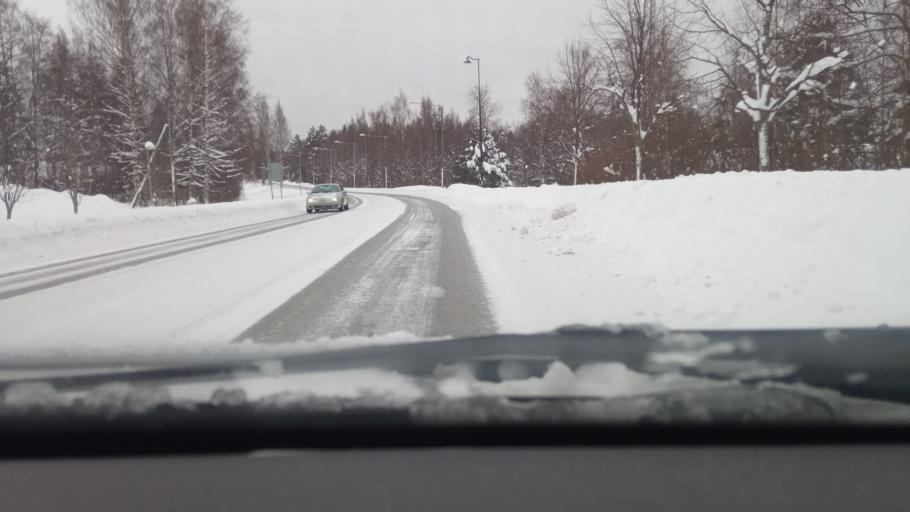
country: FI
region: Southern Ostrobothnia
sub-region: Jaerviseutu
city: Alajaervi
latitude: 62.9985
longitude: 23.8110
